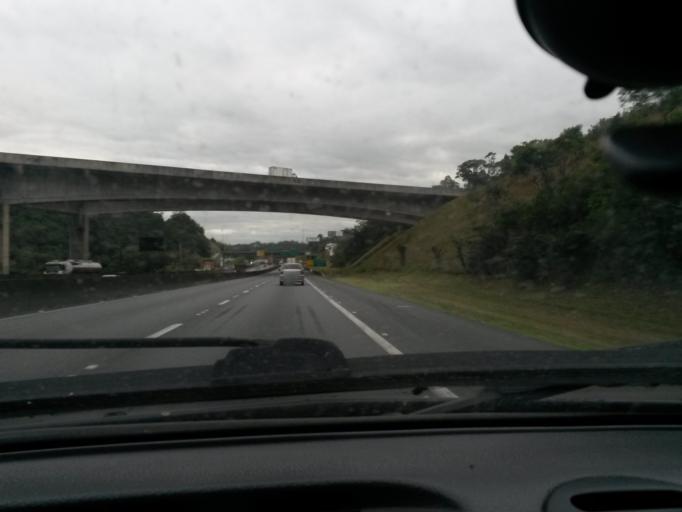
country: BR
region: Sao Paulo
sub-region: Sao Bernardo Do Campo
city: Sao Bernardo do Campo
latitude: -23.7625
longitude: -46.5341
